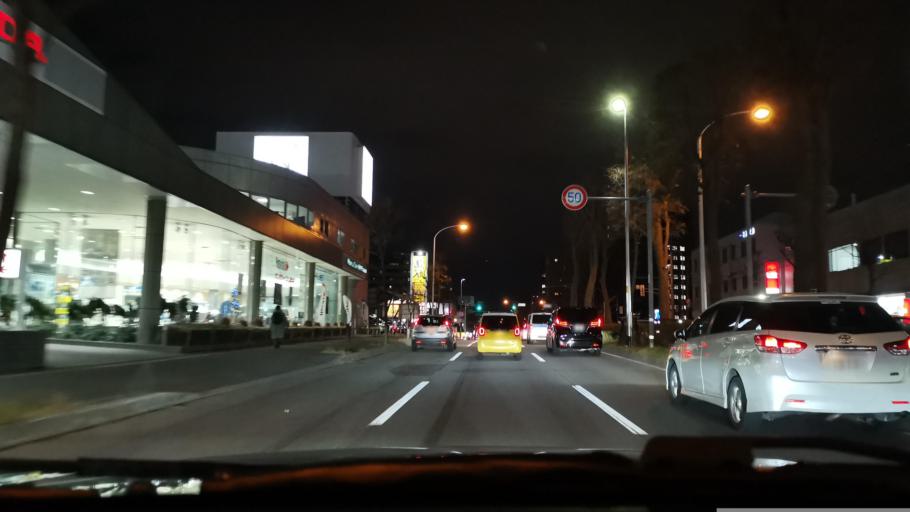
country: JP
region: Hokkaido
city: Sapporo
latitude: 43.0439
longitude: 141.4029
